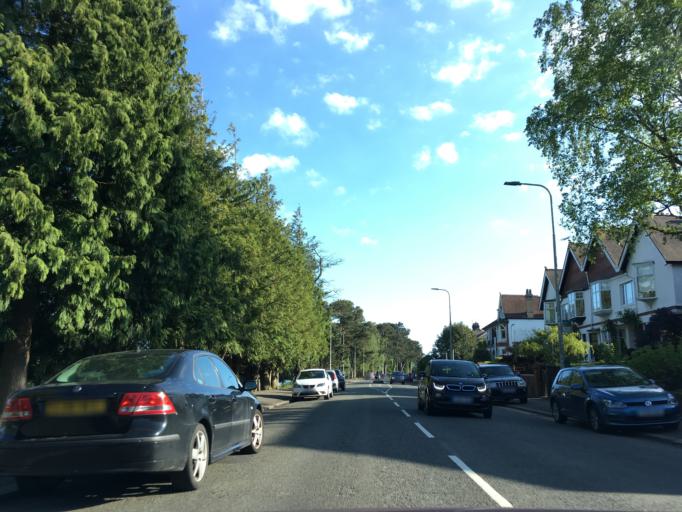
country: GB
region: Wales
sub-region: Cardiff
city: Cardiff
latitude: 51.5112
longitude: -3.1766
